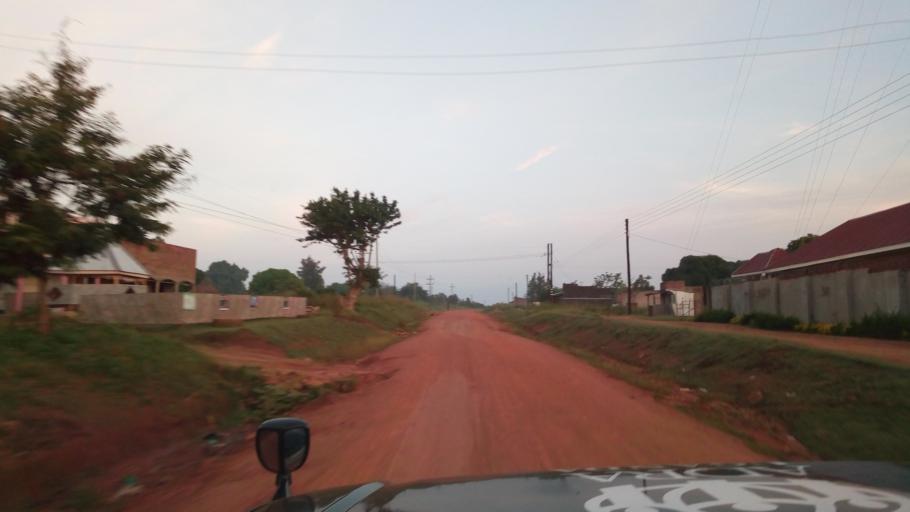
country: UG
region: Northern Region
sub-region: Adjumani District
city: Adjumani
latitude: 3.3919
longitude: 31.7896
